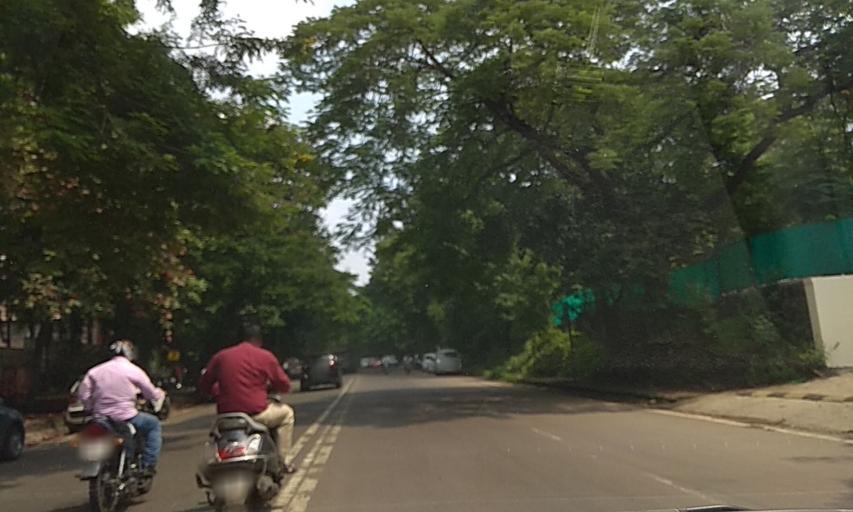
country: IN
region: Maharashtra
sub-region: Pune Division
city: Shivaji Nagar
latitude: 18.5401
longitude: 73.8187
